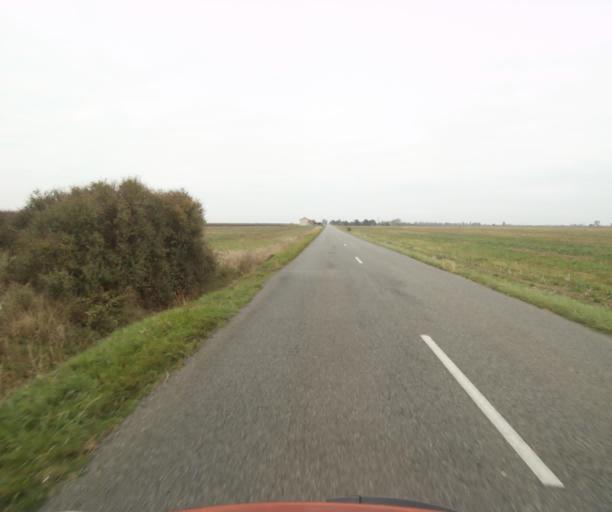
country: FR
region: Midi-Pyrenees
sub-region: Departement du Tarn-et-Garonne
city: Verdun-sur-Garonne
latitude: 43.8154
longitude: 1.1927
